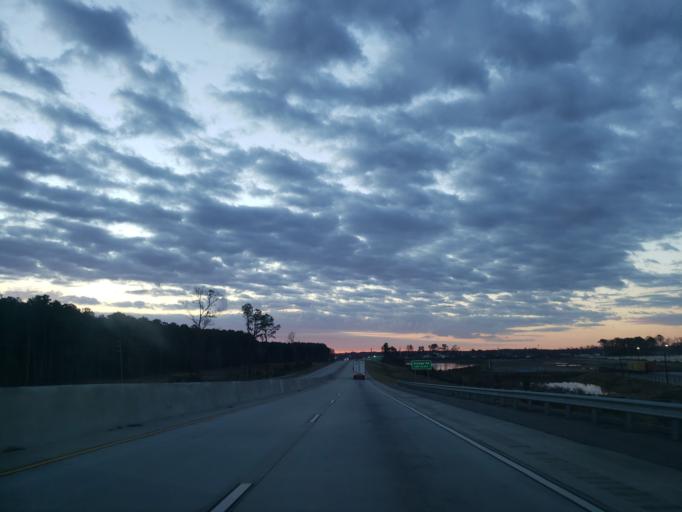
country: US
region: Georgia
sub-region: Chatham County
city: Port Wentworth
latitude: 32.1464
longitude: -81.1727
